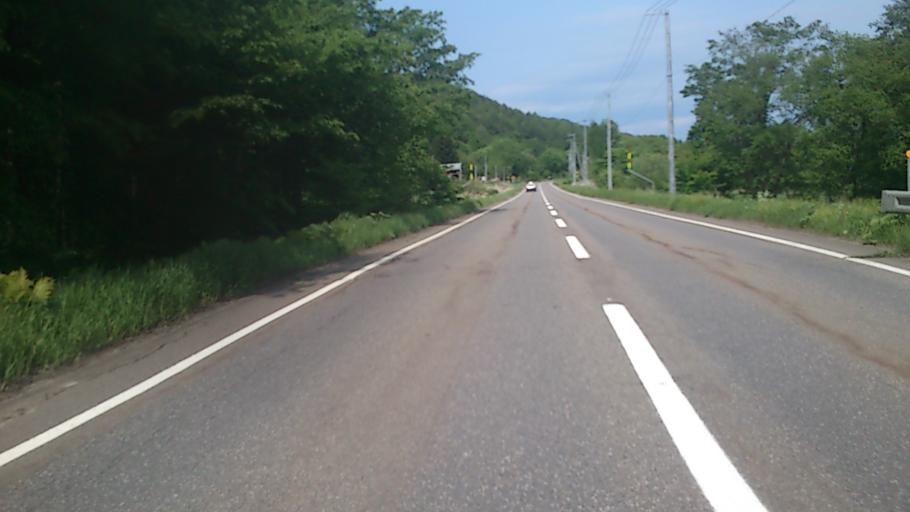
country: JP
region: Hokkaido
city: Otofuke
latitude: 43.2622
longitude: 143.5772
